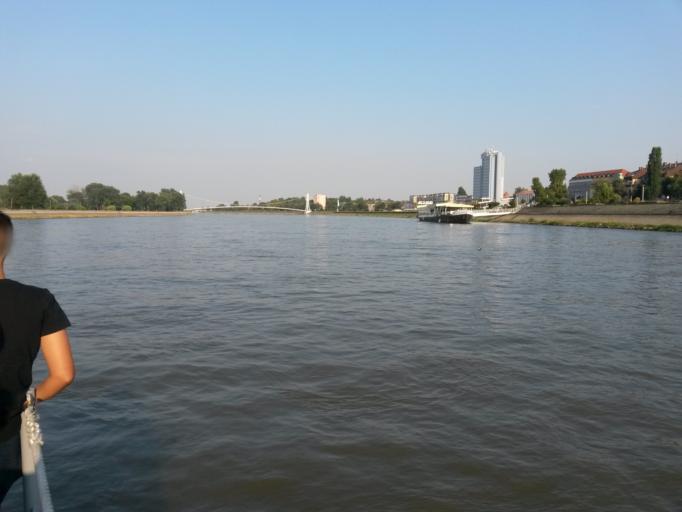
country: HR
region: Osjecko-Baranjska
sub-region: Grad Osijek
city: Osijek
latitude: 45.5652
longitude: 18.6739
